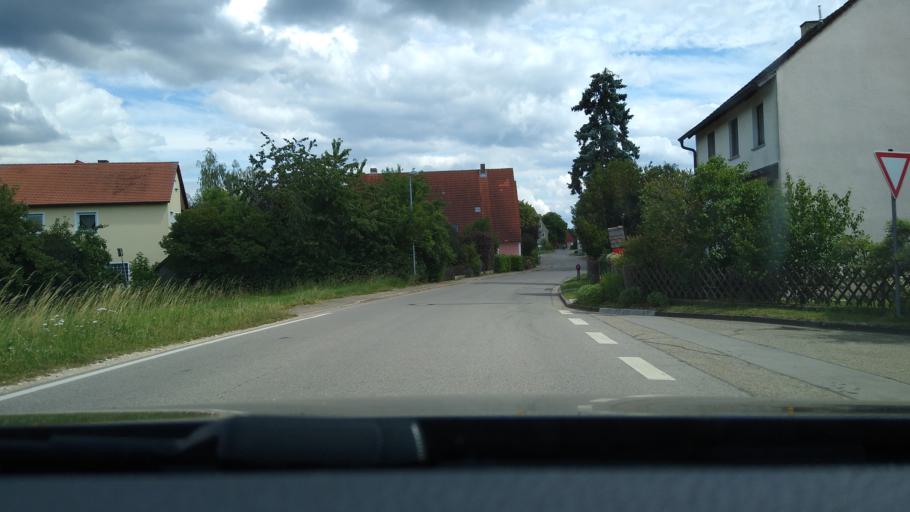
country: DE
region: Bavaria
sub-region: Regierungsbezirk Mittelfranken
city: Absberg
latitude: 49.1473
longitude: 10.8415
